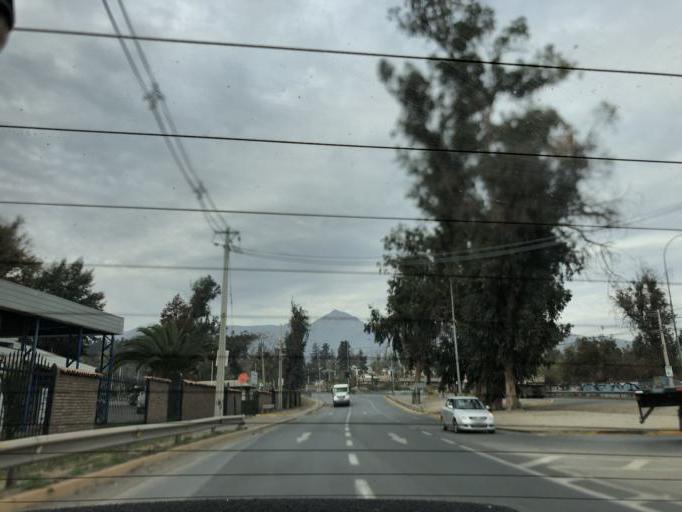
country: CL
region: Santiago Metropolitan
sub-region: Provincia de Cordillera
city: Puente Alto
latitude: -33.5976
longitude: -70.5317
